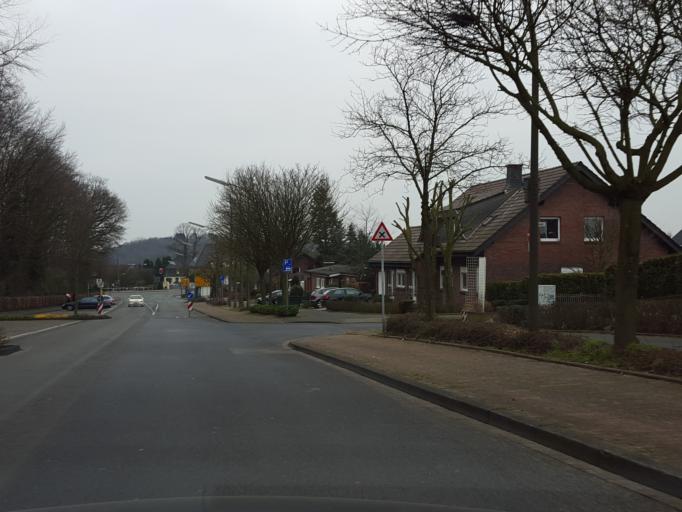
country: DE
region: North Rhine-Westphalia
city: Oer-Erkenschwick
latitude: 51.6552
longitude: 7.2501
